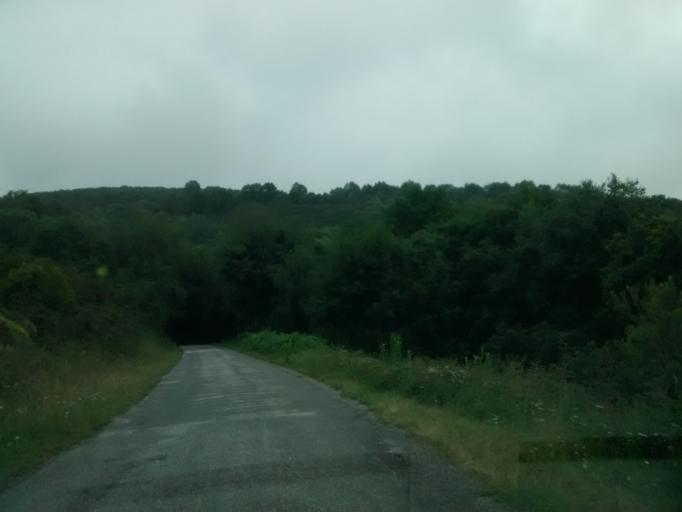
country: ES
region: Galicia
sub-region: Provincia de Ourense
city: Castro Caldelas
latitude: 42.3986
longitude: -7.3964
